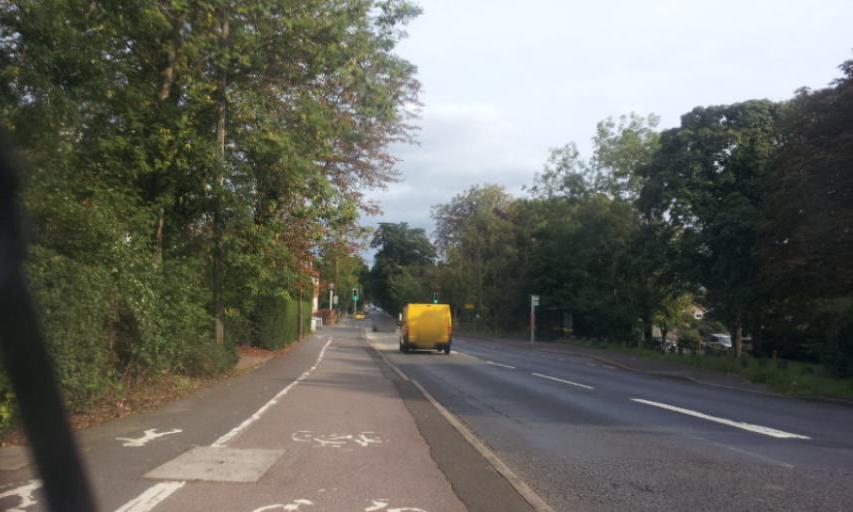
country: GB
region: England
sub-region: Kent
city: Tonbridge
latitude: 51.2137
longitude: 0.2483
